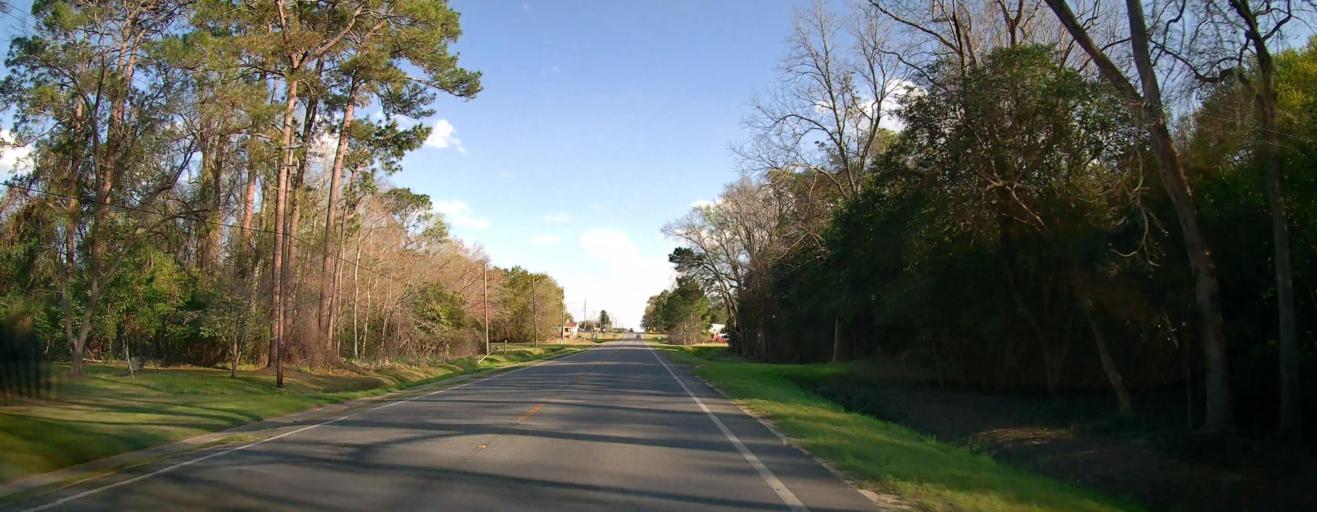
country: US
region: Georgia
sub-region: Toombs County
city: Lyons
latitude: 32.1983
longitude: -82.3137
